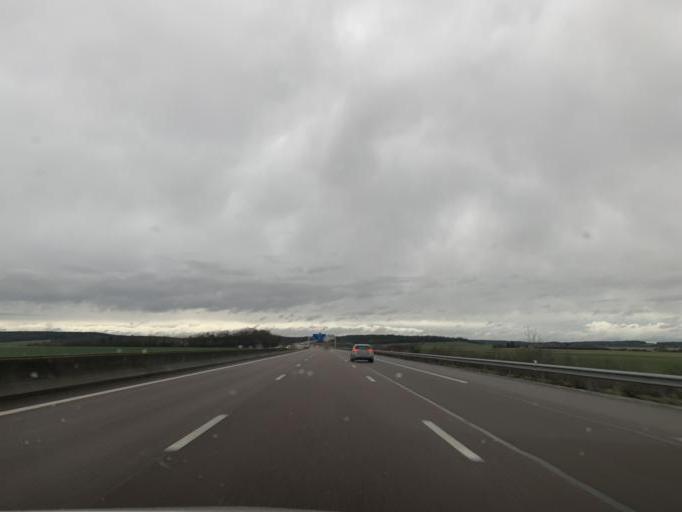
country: FR
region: Bourgogne
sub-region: Departement de la Cote-d'Or
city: Selongey
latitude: 47.5335
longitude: 5.1992
